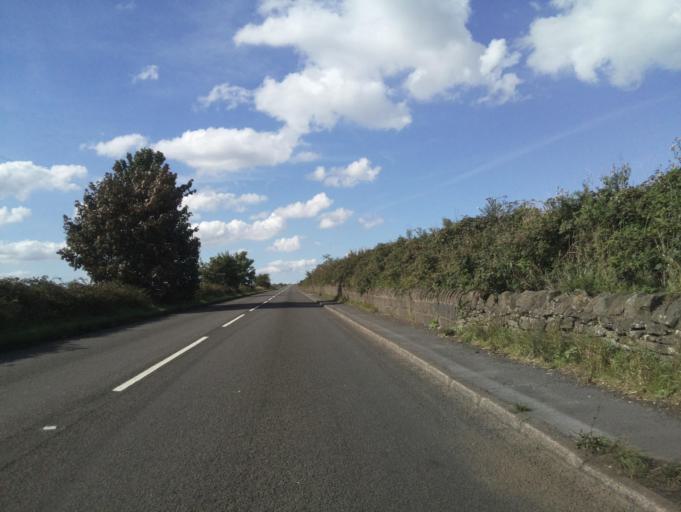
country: GB
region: Scotland
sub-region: Stirling
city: Plean
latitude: 56.0743
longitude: -3.8873
